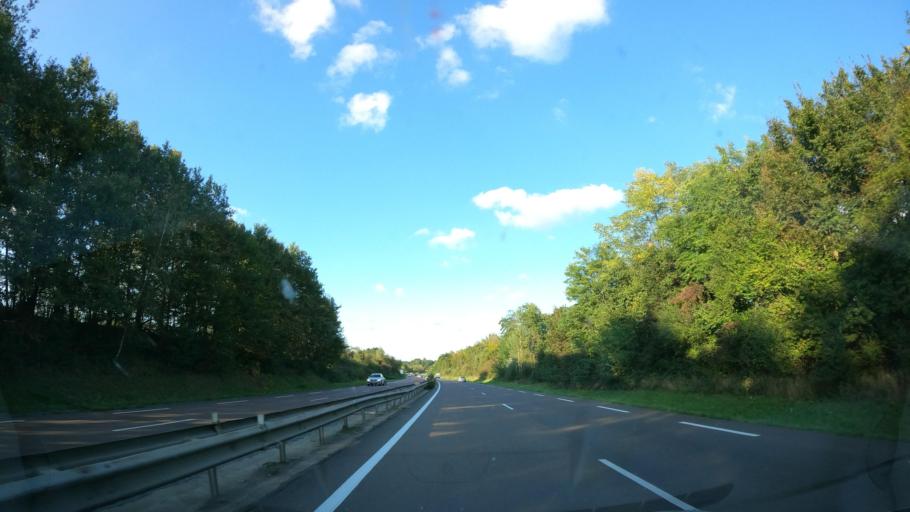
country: FR
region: Bourgogne
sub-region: Departement de Saone-et-Loire
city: Montceau-les-Mines
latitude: 46.6737
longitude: 4.3451
